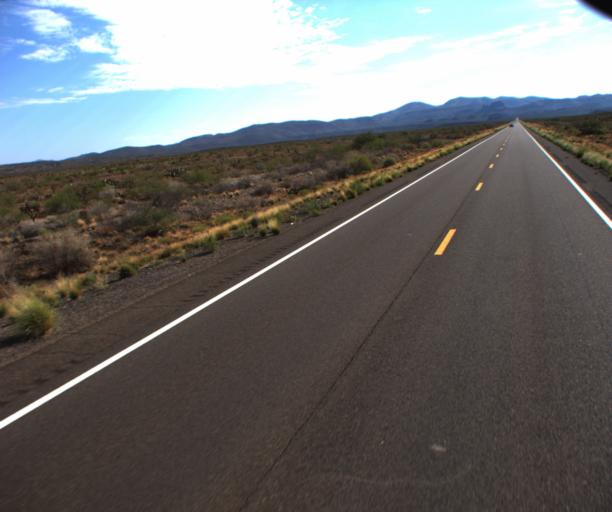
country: US
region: Arizona
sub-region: Graham County
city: Safford
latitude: 32.8212
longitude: -109.4749
